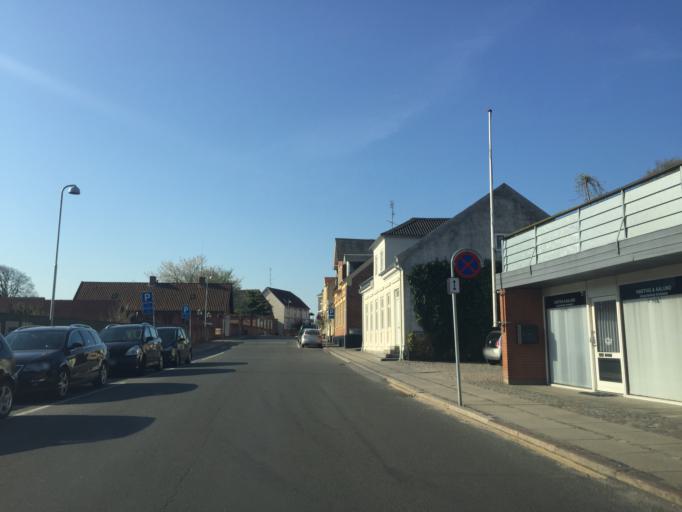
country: DK
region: South Denmark
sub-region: Svendborg Kommune
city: Svendborg
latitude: 55.0562
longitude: 10.6125
